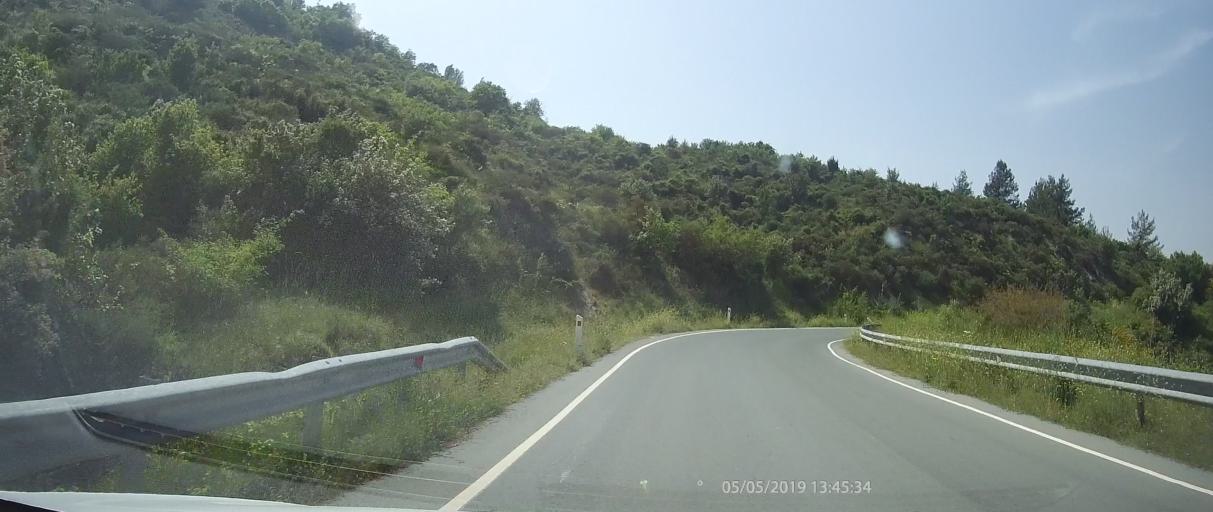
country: CY
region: Limassol
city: Pachna
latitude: 34.8703
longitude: 32.7807
